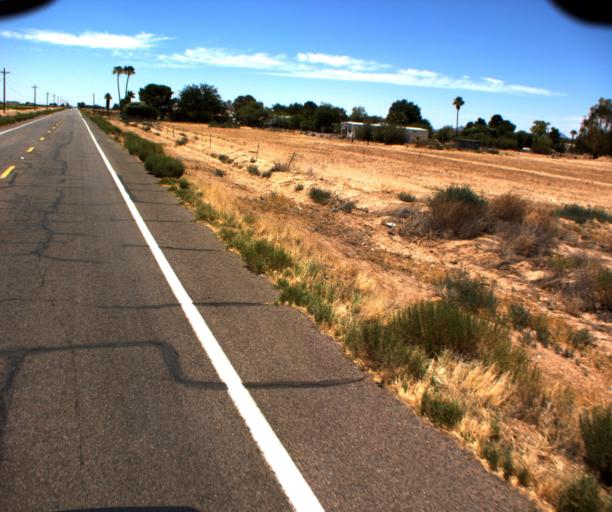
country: US
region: Arizona
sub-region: Pinal County
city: Coolidge
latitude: 32.8795
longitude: -111.5188
